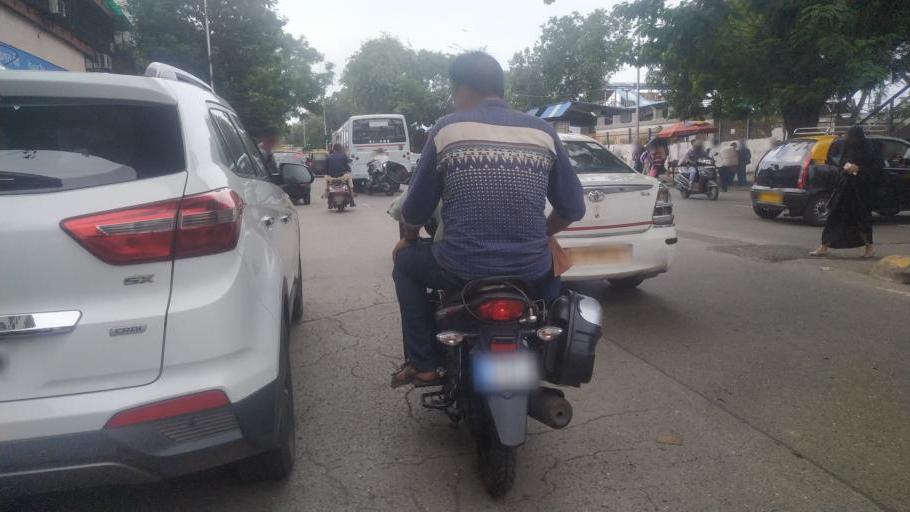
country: IN
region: Maharashtra
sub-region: Mumbai Suburban
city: Mumbai
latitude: 19.0388
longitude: 72.8471
